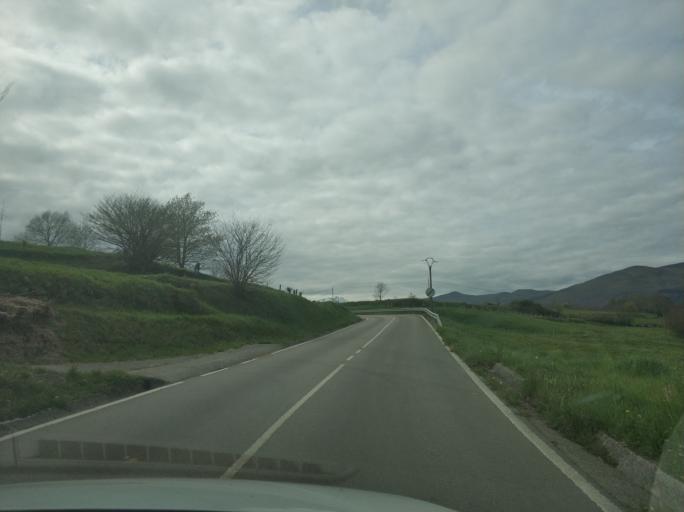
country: ES
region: Cantabria
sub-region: Provincia de Cantabria
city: Ruente
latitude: 43.2378
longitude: -4.2820
